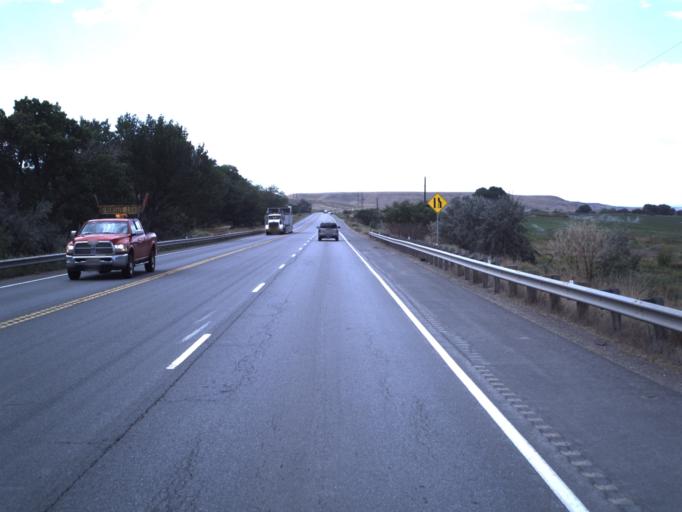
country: US
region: Utah
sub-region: Duchesne County
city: Duchesne
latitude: 40.1533
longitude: -110.2299
